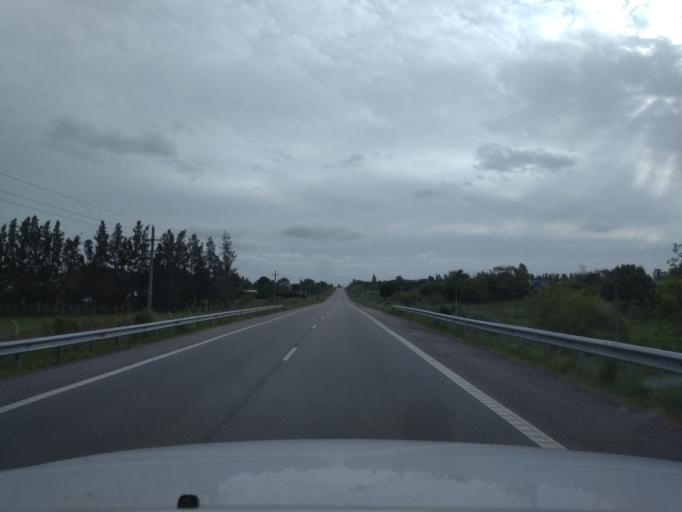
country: UY
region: Canelones
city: Joaquin Suarez
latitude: -34.6948
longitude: -56.0331
